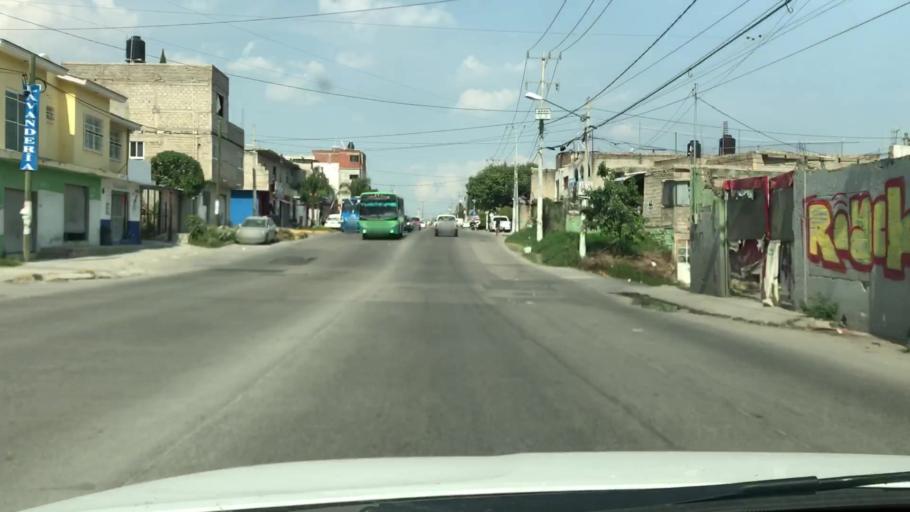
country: MX
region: Jalisco
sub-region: Tlajomulco de Zuniga
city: Palomar
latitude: 20.6514
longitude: -103.4555
